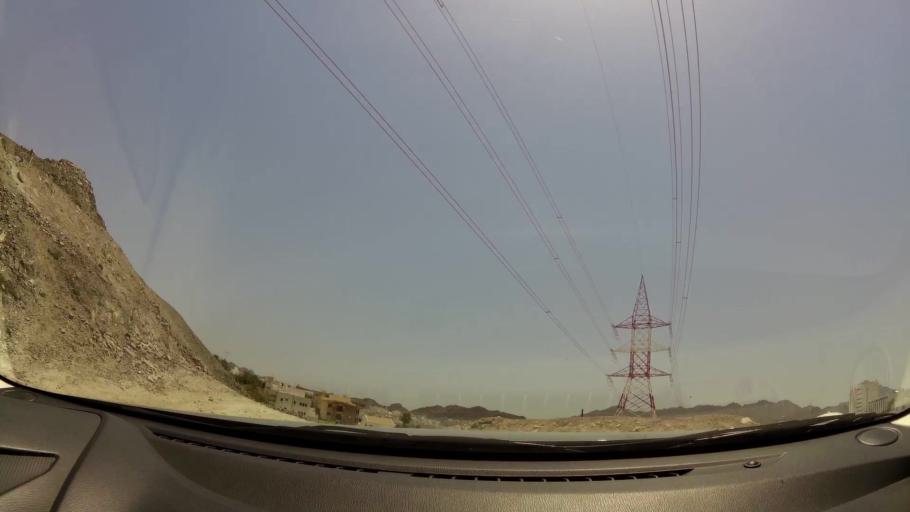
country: OM
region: Muhafazat Masqat
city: Muscat
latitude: 23.6081
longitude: 58.5355
